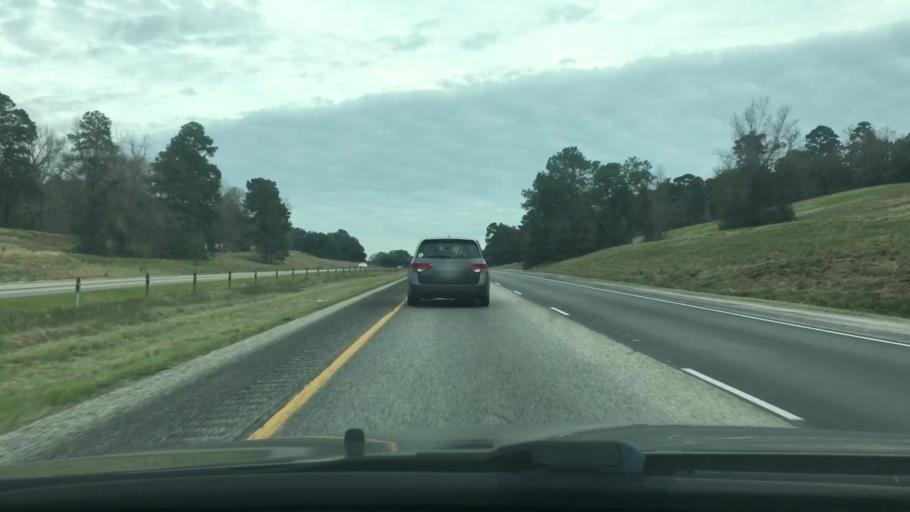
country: US
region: Texas
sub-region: Walker County
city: Huntsville
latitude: 30.8184
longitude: -95.7008
